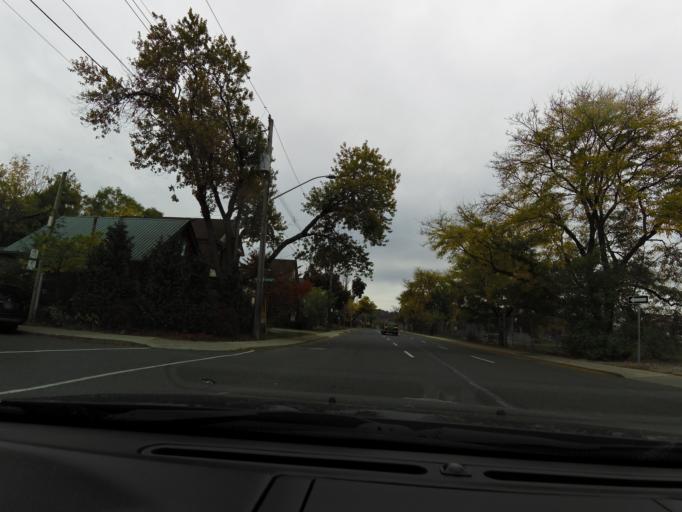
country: CA
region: Ontario
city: Hamilton
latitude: 43.2621
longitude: -79.8990
